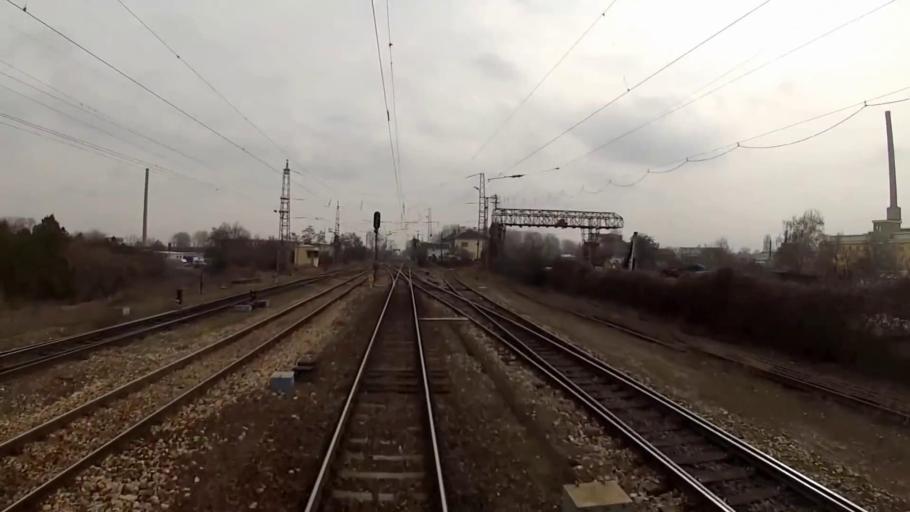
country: BG
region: Sofiya
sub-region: Obshtina Elin Pelin
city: Elin Pelin
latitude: 42.6542
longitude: 23.4605
